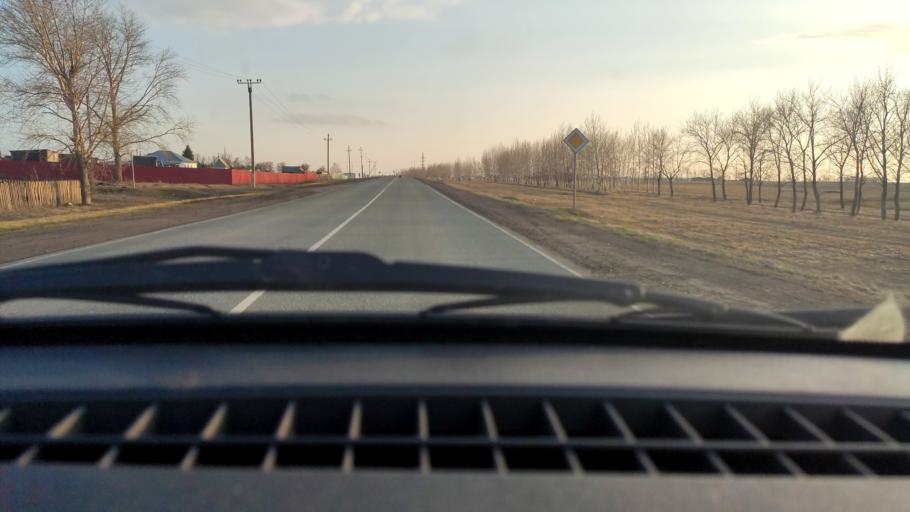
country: RU
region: Bashkortostan
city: Davlekanovo
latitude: 54.3885
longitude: 55.2008
